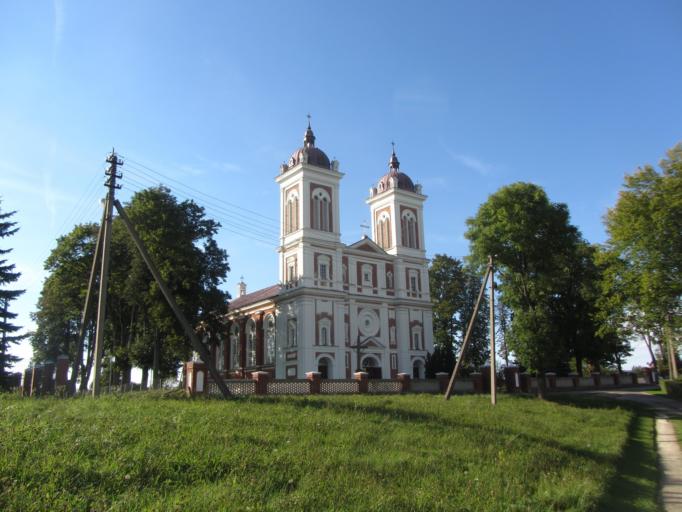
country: LT
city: Vilkija
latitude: 55.0811
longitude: 23.4155
